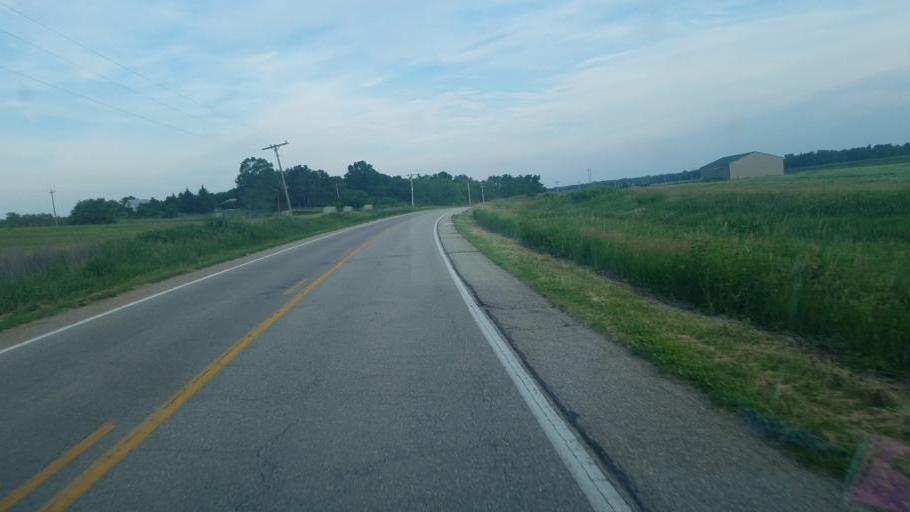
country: US
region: Iowa
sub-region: Benton County
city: Belle Plaine
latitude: 41.9475
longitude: -92.4174
